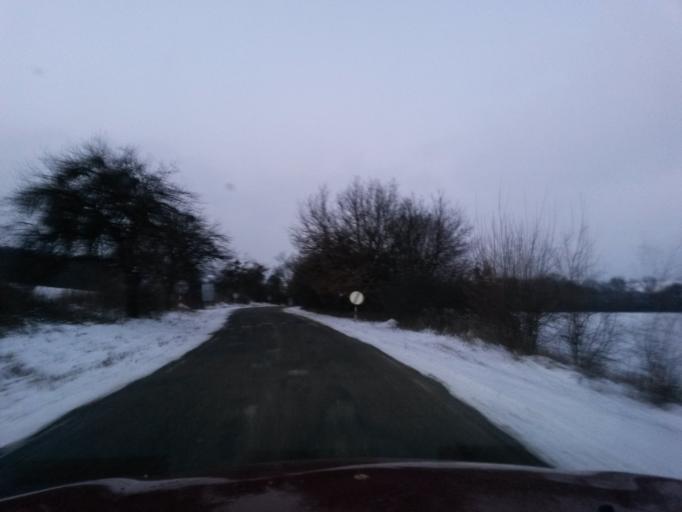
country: SK
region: Kosicky
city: Kosice
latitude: 48.7343
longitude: 21.3273
